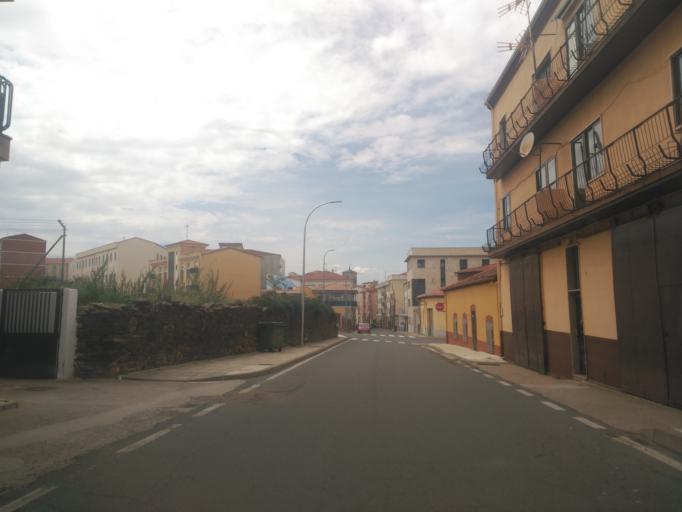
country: ES
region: Castille and Leon
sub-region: Provincia de Salamanca
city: Guijuelo
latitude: 40.5542
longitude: -5.6692
